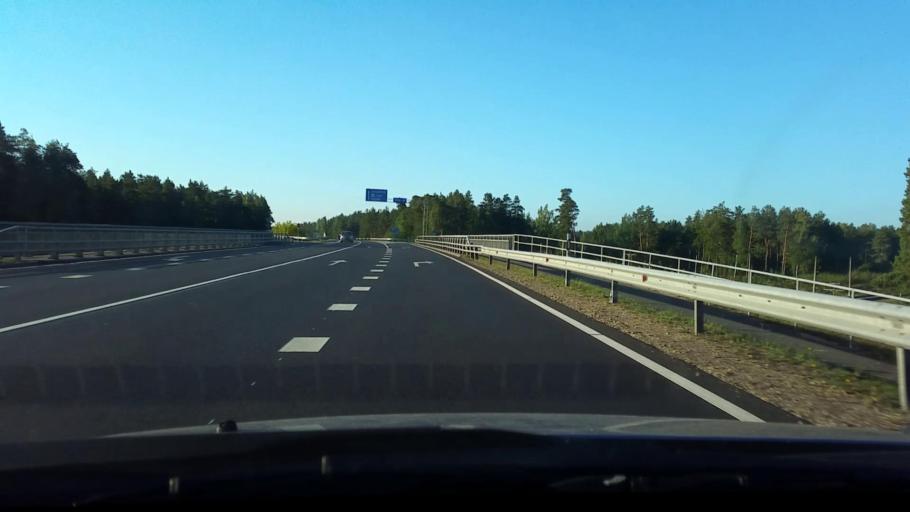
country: LV
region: Riga
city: Bergi
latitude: 57.0112
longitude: 24.3069
